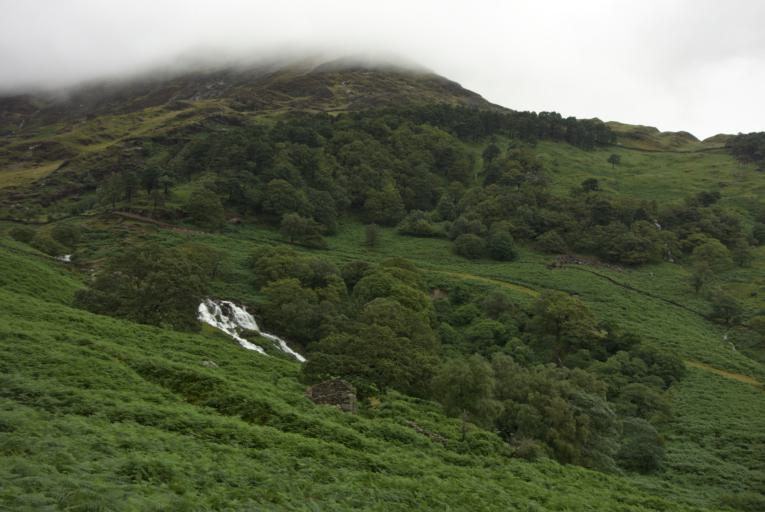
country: GB
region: Wales
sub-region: Gwynedd
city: Llanberis
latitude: 53.0418
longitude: -4.0556
